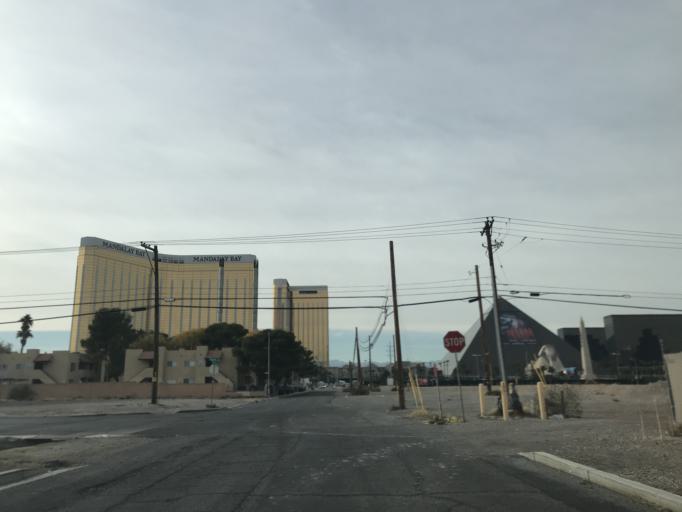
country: US
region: Nevada
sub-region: Clark County
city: Paradise
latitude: 36.0936
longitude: -115.1679
